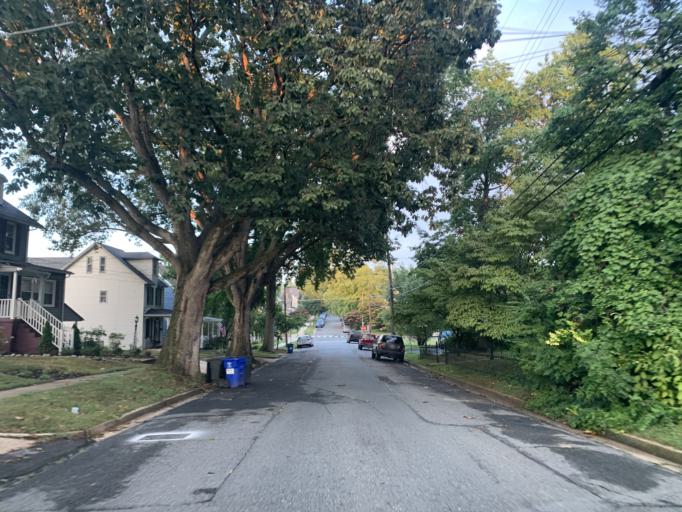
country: US
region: Maryland
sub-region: Harford County
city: Havre de Grace
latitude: 39.5541
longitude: -76.0985
